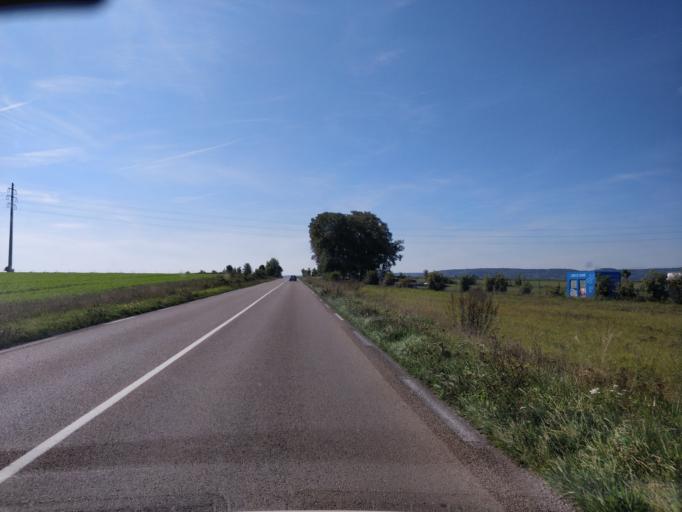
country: FR
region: Champagne-Ardenne
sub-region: Departement de l'Aube
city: Saint-Germain
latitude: 48.2386
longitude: 4.0208
